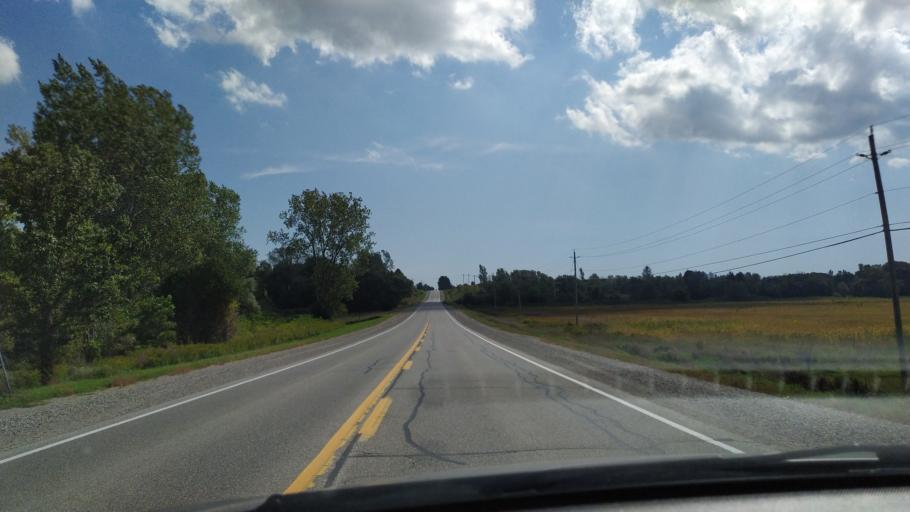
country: CA
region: Ontario
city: Ingersoll
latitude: 43.1413
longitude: -80.8940
